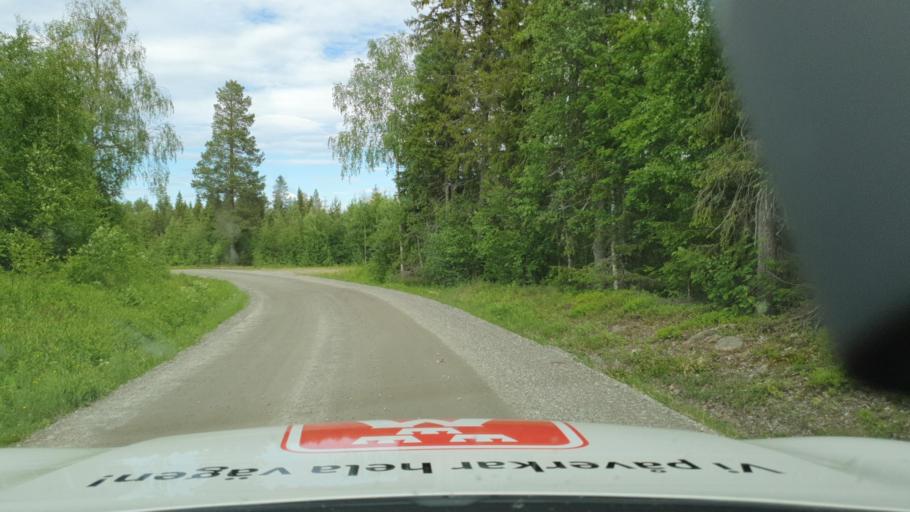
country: SE
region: Vaesterbotten
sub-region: Norsjo Kommun
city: Norsjoe
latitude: 64.8076
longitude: 19.6700
